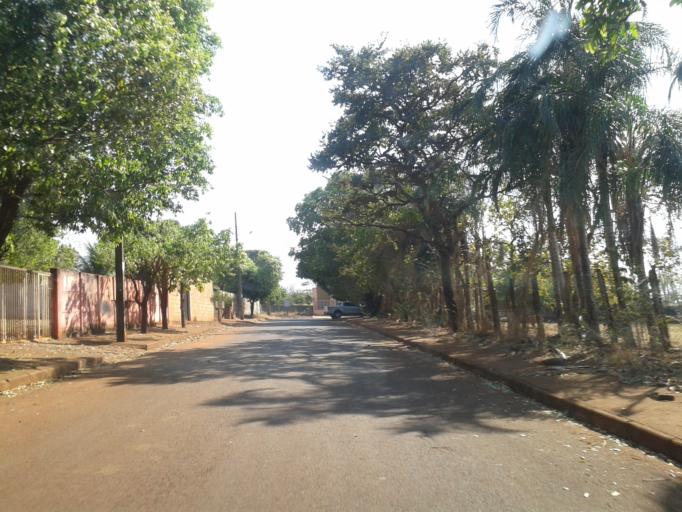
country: BR
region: Minas Gerais
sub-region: Ituiutaba
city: Ituiutaba
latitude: -18.9601
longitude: -49.4785
